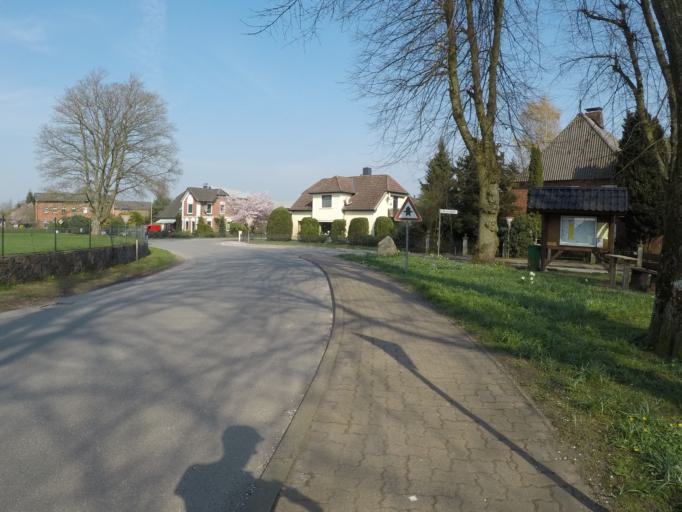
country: DE
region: Schleswig-Holstein
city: Gross Niendorf
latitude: 53.8455
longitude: 10.2450
